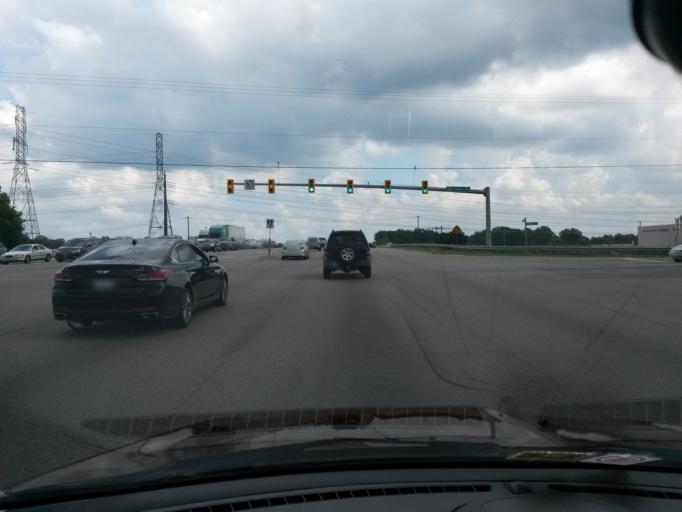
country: US
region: Virginia
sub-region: Chesterfield County
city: Chester
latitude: 37.3536
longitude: -77.3969
